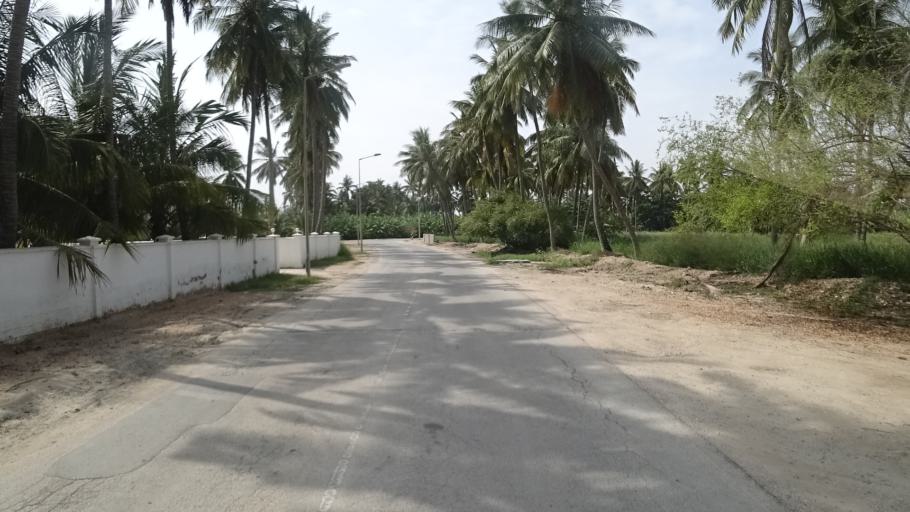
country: OM
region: Zufar
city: Salalah
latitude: 17.0144
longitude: 54.1528
